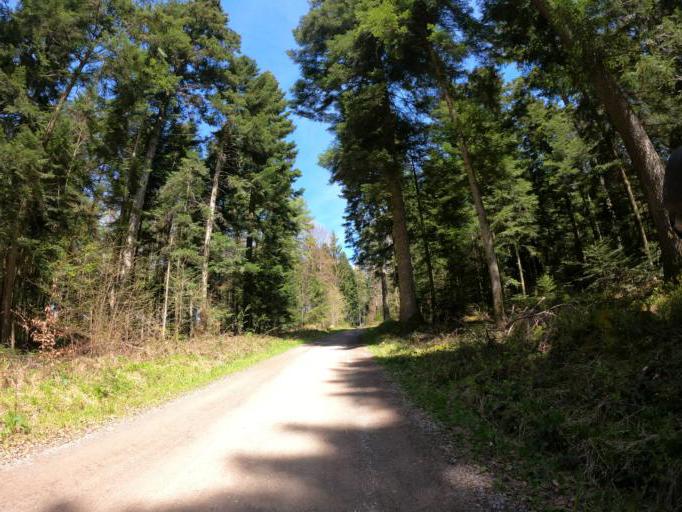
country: DE
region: Baden-Wuerttemberg
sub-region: Karlsruhe Region
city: Schomberg
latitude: 48.7956
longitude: 8.6333
